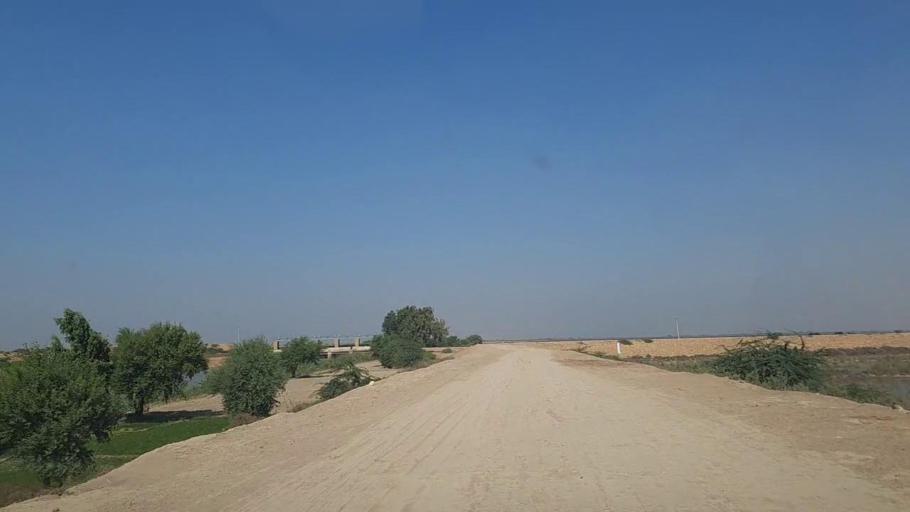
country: PK
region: Sindh
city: Daro Mehar
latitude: 24.9128
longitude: 68.0782
